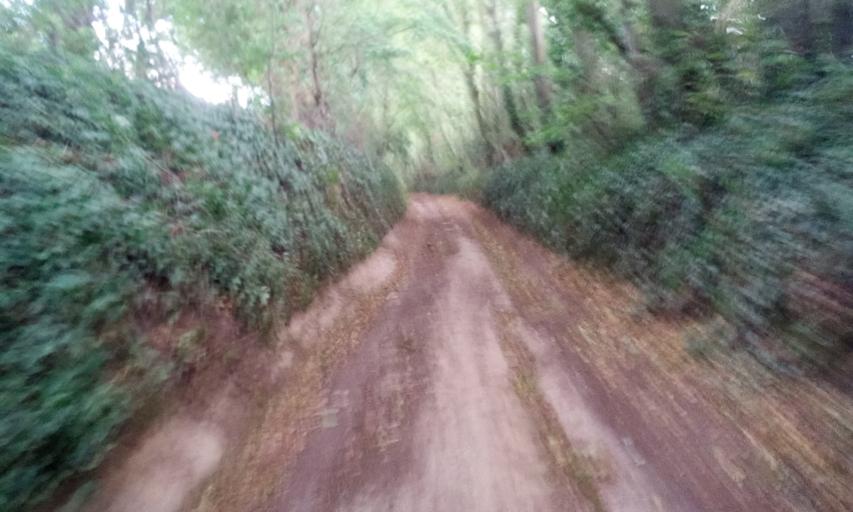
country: FR
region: Lower Normandy
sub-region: Departement du Calvados
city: Courseulles-sur-Mer
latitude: 49.2994
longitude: -0.4772
